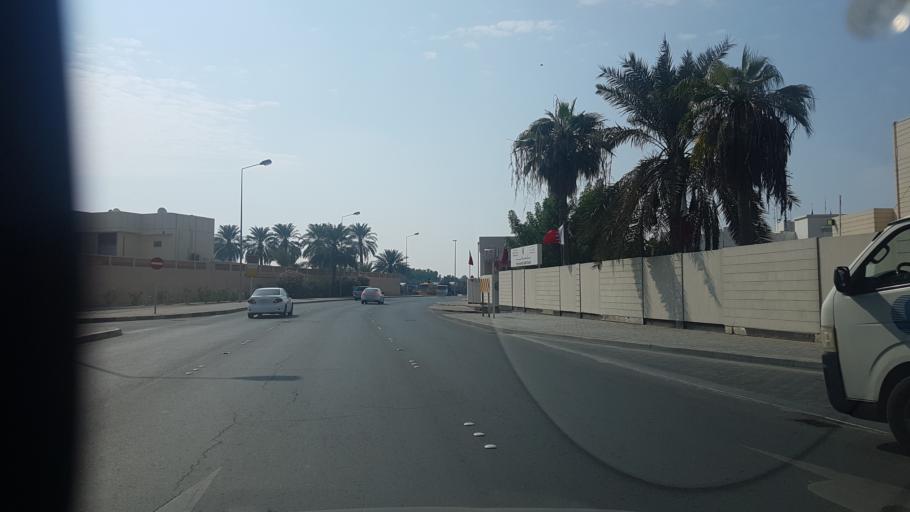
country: BH
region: Manama
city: Jidd Hafs
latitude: 26.2278
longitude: 50.5654
